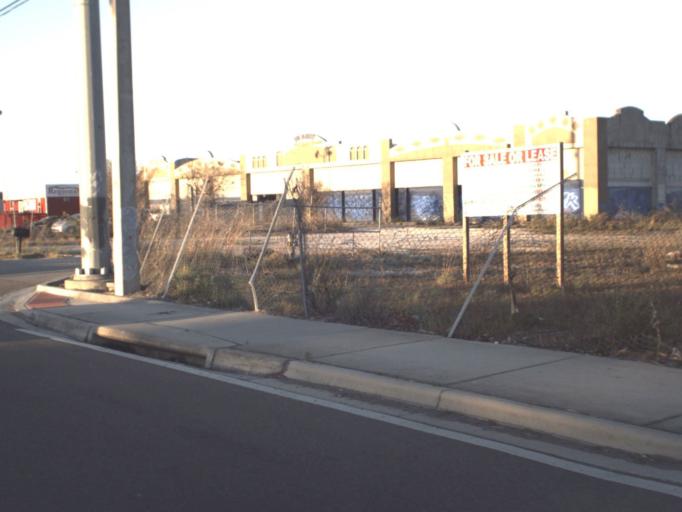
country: US
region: Florida
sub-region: Orange County
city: Azalea Park
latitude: 28.5552
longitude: -81.3106
